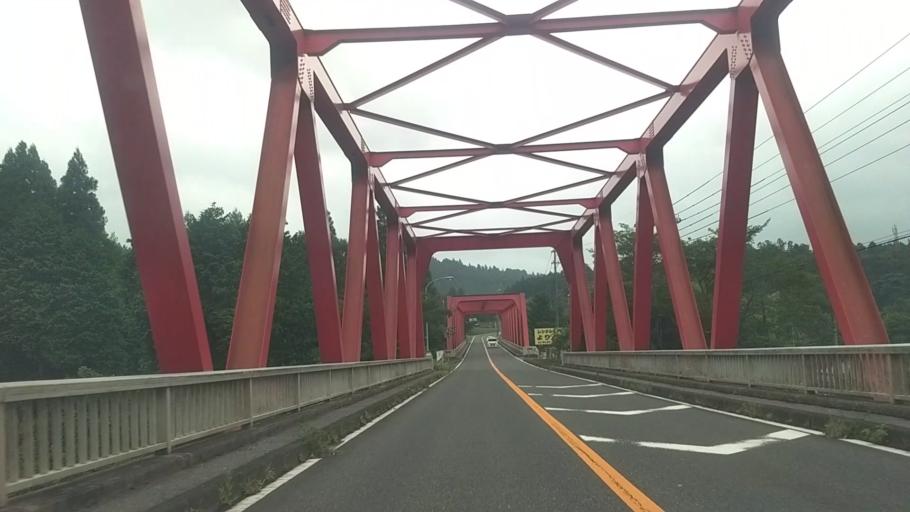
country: JP
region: Chiba
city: Kawaguchi
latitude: 35.2218
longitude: 140.0725
